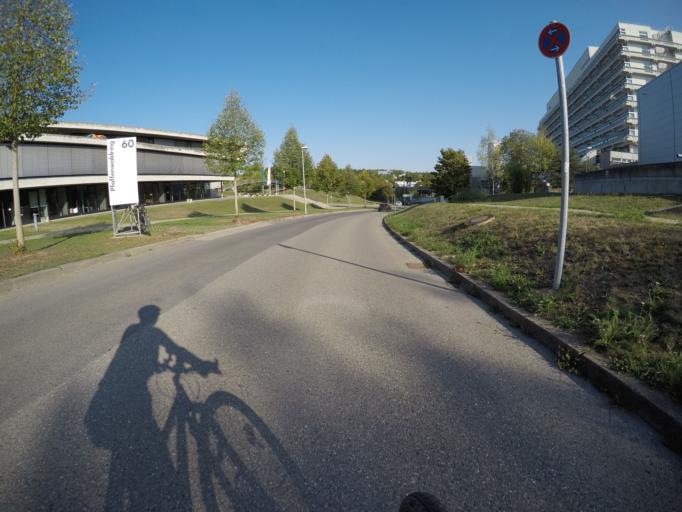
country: DE
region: Baden-Wuerttemberg
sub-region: Regierungsbezirk Stuttgart
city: Gerlingen
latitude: 48.7439
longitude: 9.1028
